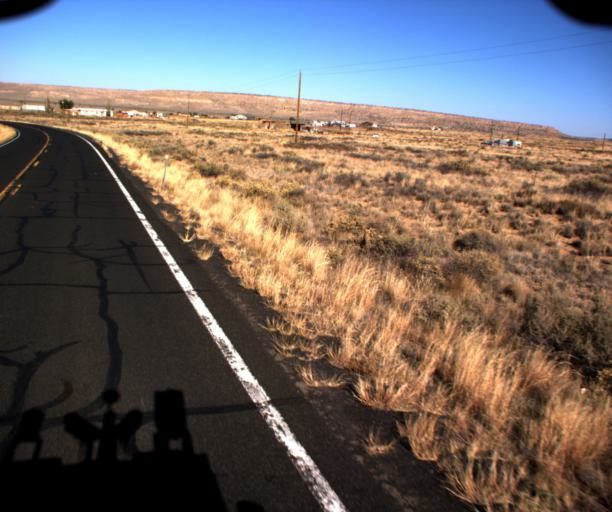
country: US
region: Arizona
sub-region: Navajo County
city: First Mesa
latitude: 35.8379
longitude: -110.3033
